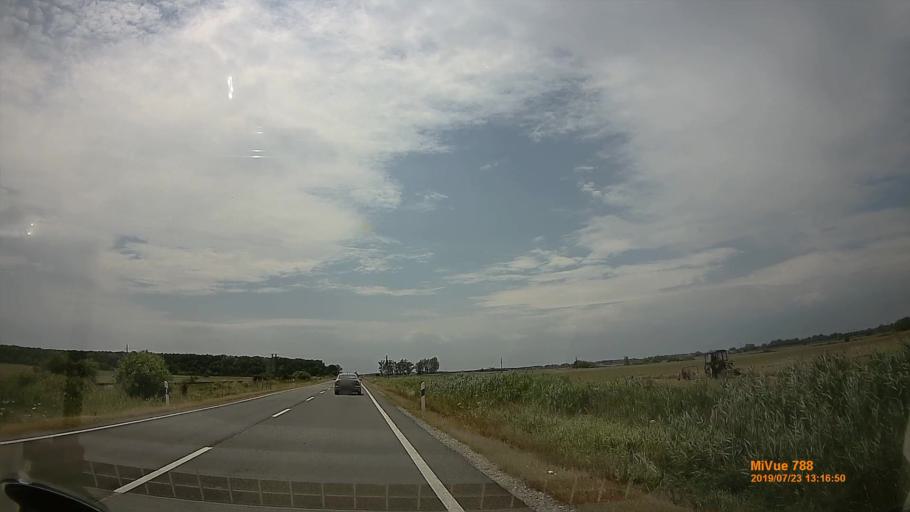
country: HU
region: Hajdu-Bihar
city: Polgar
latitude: 47.9055
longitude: 21.1648
